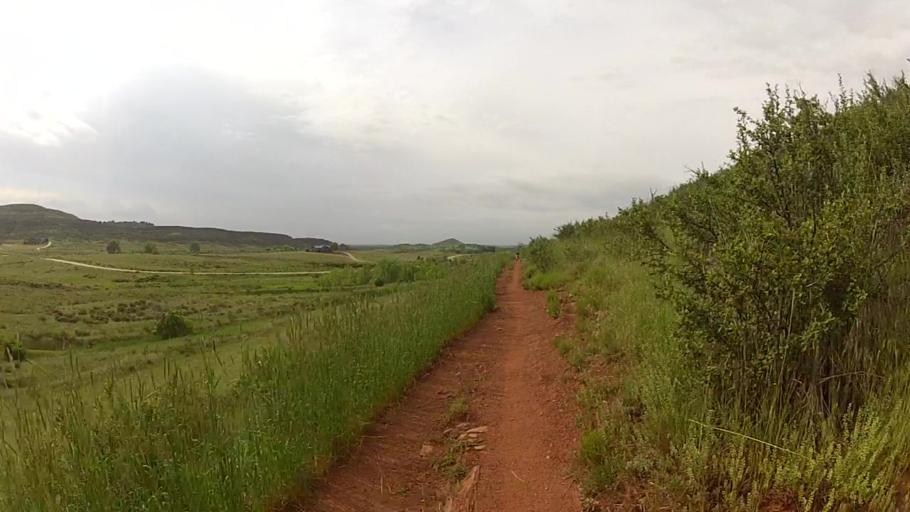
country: US
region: Colorado
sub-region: Larimer County
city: Loveland
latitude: 40.4153
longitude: -105.1543
